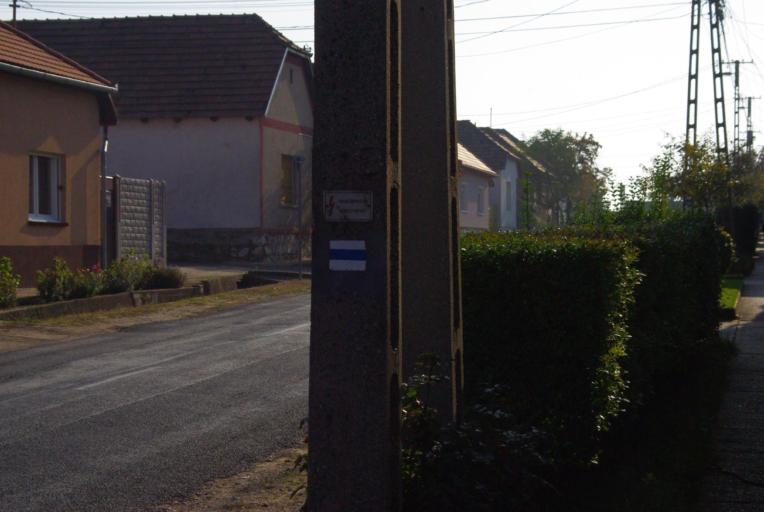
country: HU
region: Komarom-Esztergom
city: Kesztolc
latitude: 47.7166
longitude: 18.7826
